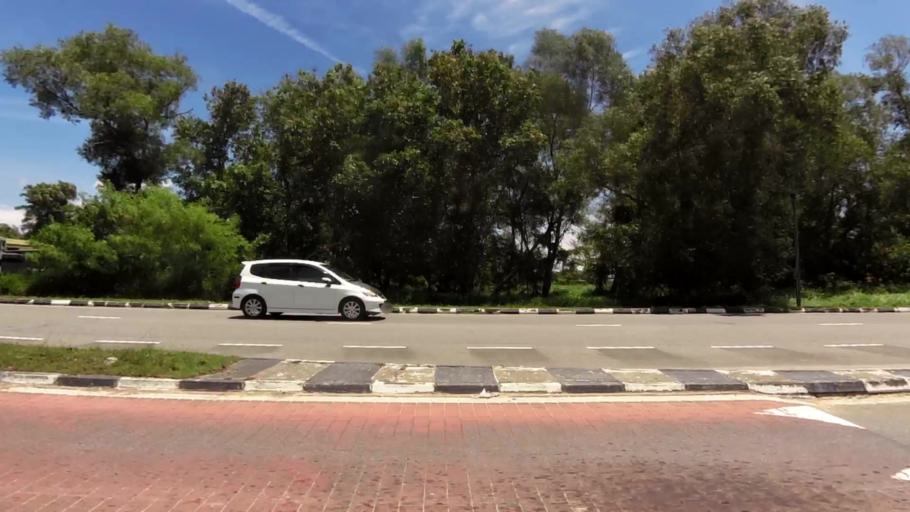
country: BN
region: Brunei and Muara
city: Bandar Seri Begawan
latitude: 4.9350
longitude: 114.9392
